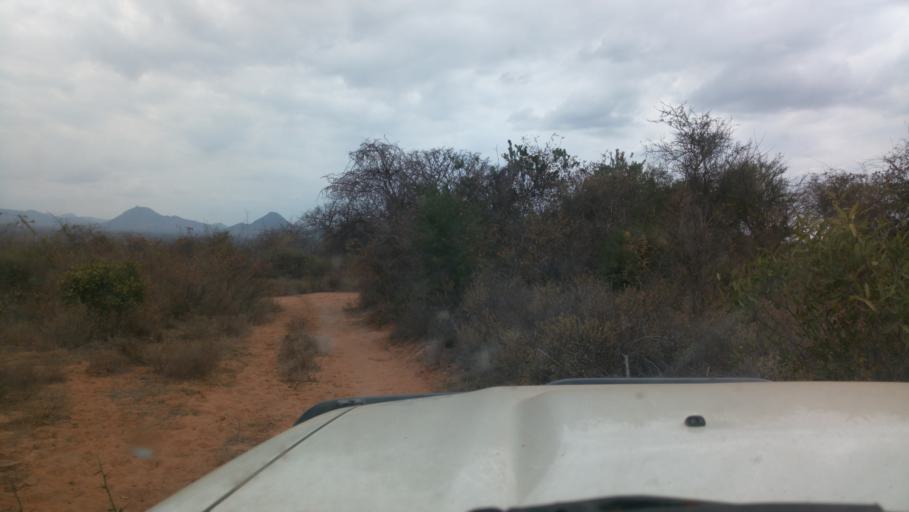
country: KE
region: Kitui
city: Kitui
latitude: -1.8441
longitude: 38.3921
